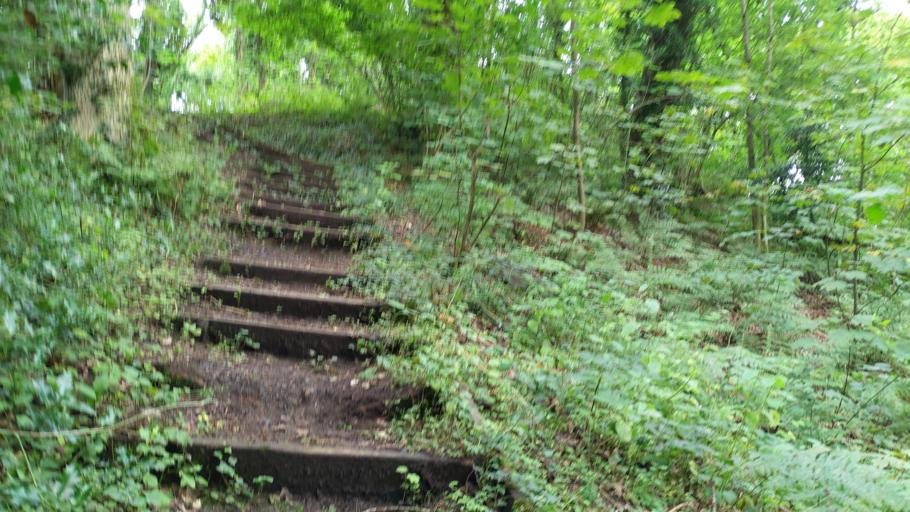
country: GB
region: England
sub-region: Lancashire
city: Coppull
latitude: 53.6369
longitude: -2.6408
